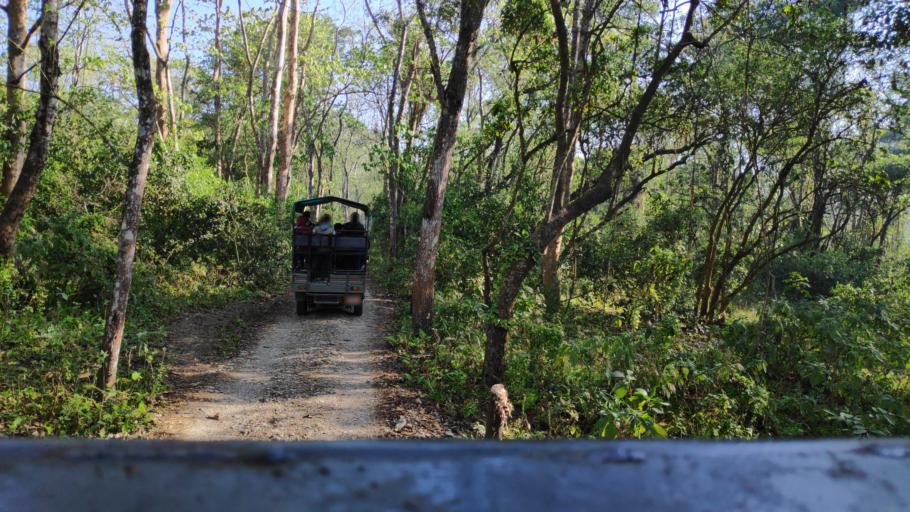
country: NP
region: Central Region
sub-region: Narayani Zone
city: Bharatpur
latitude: 27.5615
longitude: 84.5369
